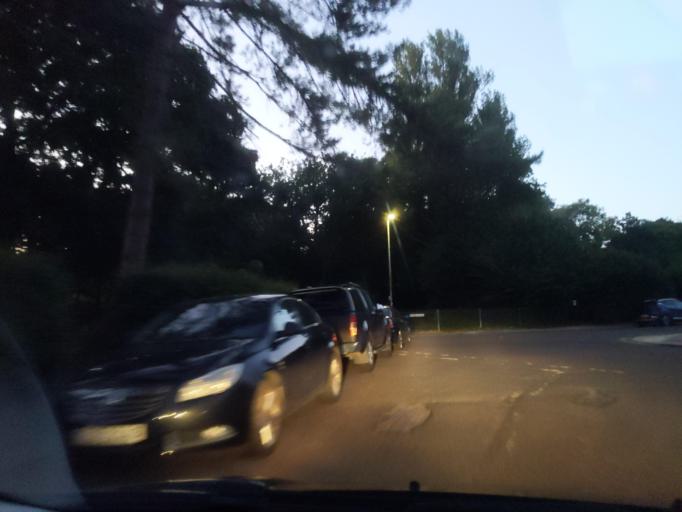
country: GB
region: England
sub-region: Plymouth
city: Plymouth
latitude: 50.3882
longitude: -4.1440
